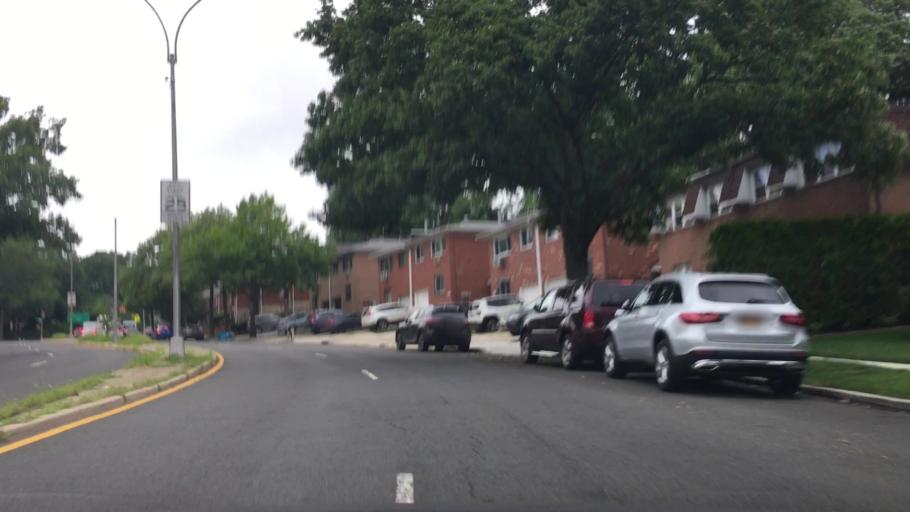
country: US
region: New York
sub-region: Nassau County
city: Lake Success
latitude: 40.7525
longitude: -73.7212
